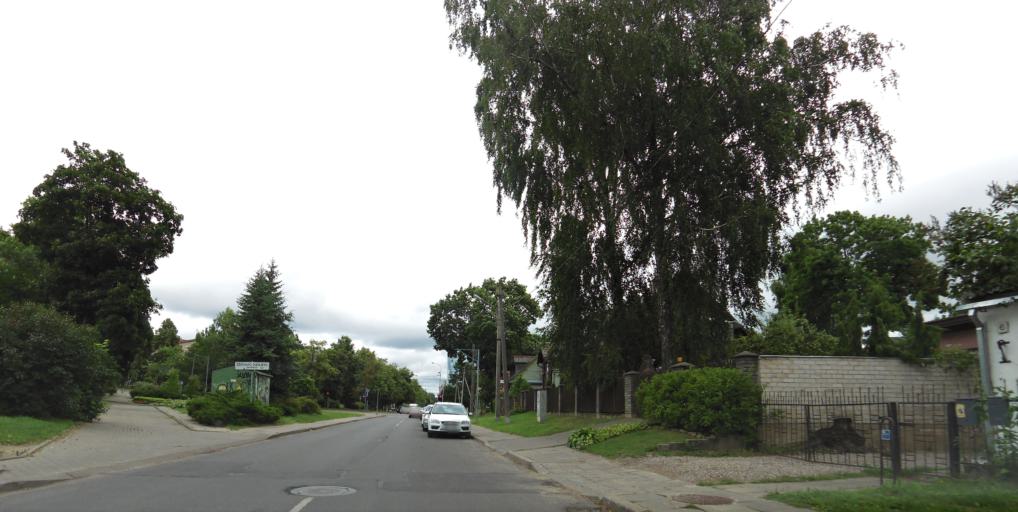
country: LT
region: Vilnius County
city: Seskine
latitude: 54.6951
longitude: 25.2546
